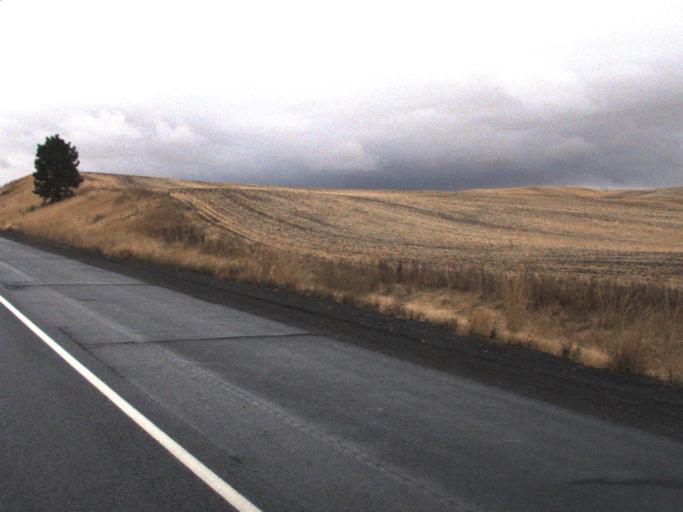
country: US
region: Washington
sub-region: Spokane County
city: Cheney
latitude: 47.4109
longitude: -117.3917
